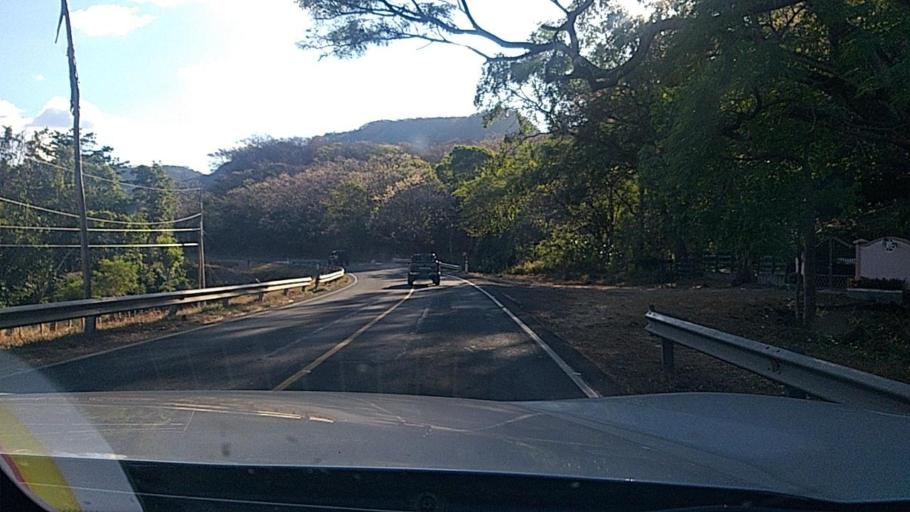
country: NI
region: Esteli
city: Condega
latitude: 13.2769
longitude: -86.3513
